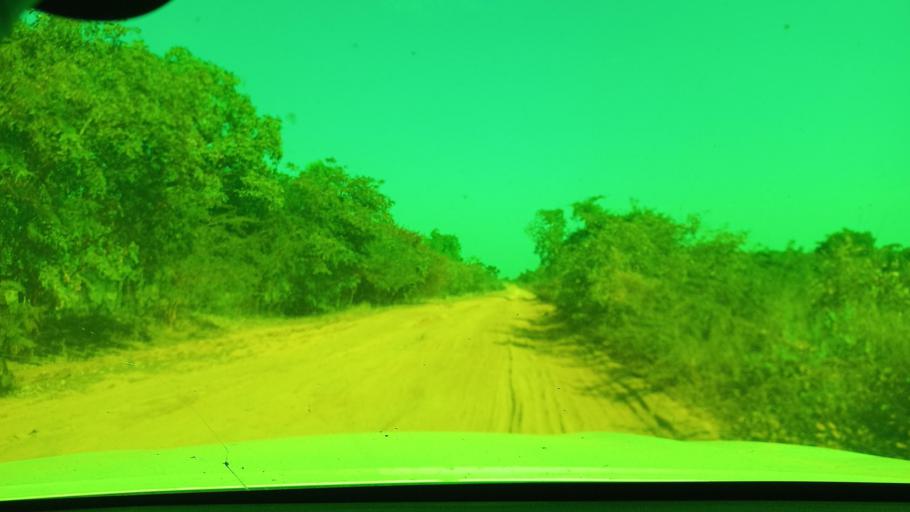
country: ML
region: Bamako
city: Bamako
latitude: 12.3971
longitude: -7.9886
